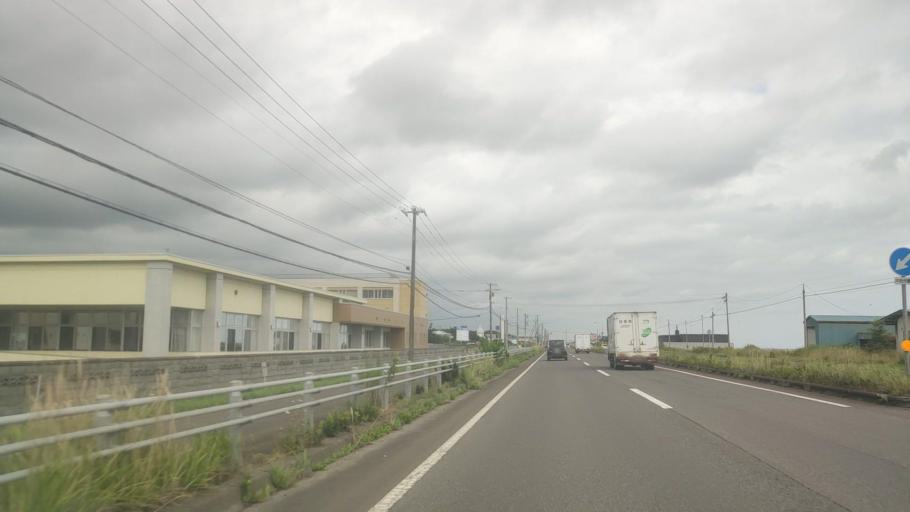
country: JP
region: Hokkaido
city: Shiraoi
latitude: 42.4705
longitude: 141.2304
